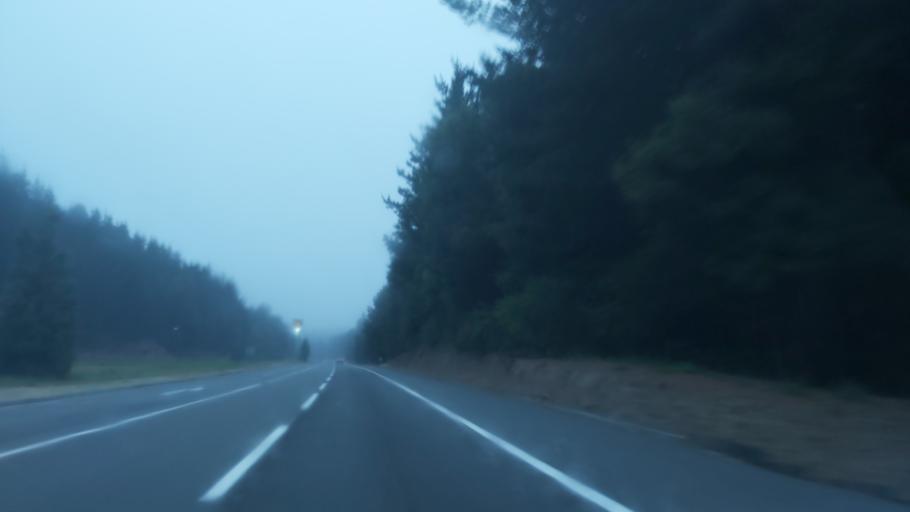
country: CL
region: Biobio
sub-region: Provincia de Concepcion
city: Penco
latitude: -36.7471
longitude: -72.9197
